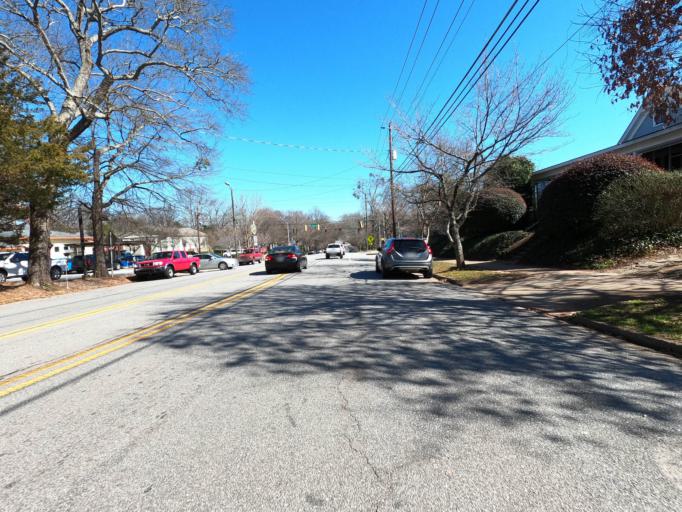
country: US
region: Georgia
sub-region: Clarke County
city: Athens
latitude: 33.9660
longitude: -83.3936
